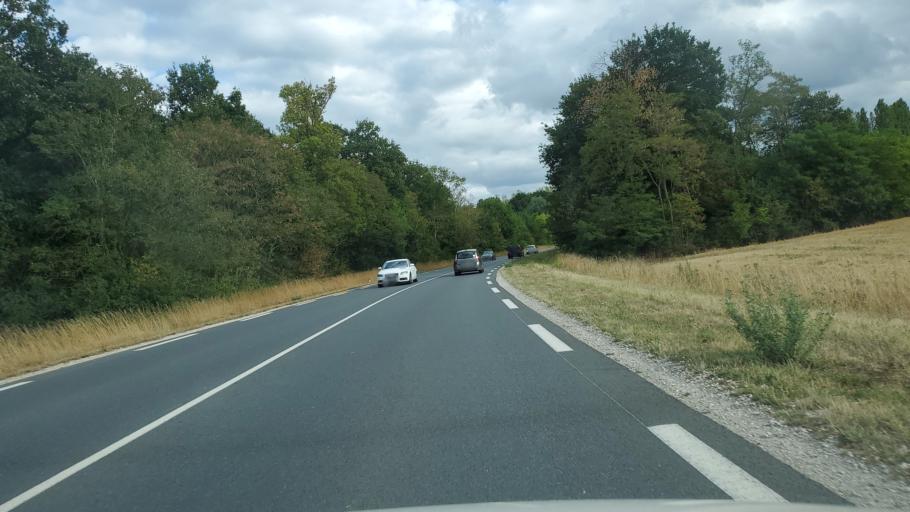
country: FR
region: Ile-de-France
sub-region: Departement de Seine-et-Marne
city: Villeneuve-le-Comte
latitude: 48.8211
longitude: 2.8414
